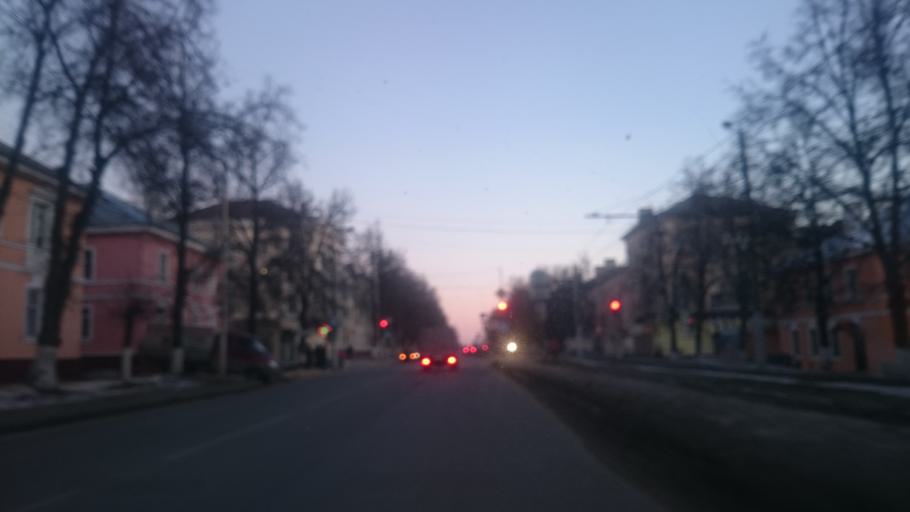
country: RU
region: Tula
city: Tula
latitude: 54.1823
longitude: 37.7026
